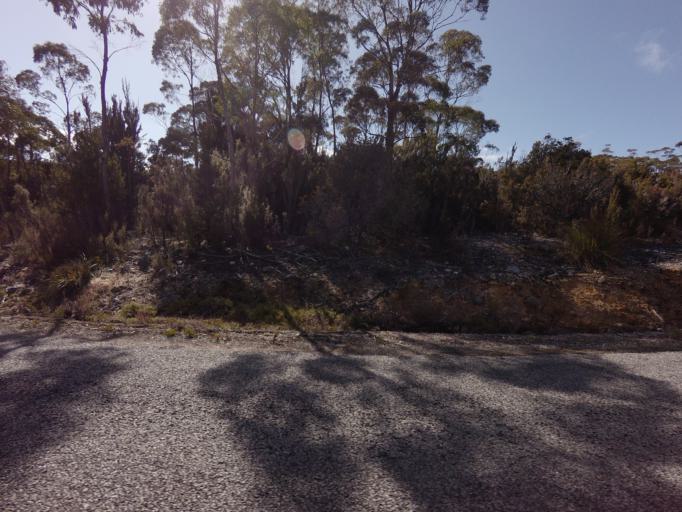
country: AU
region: Tasmania
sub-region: Huon Valley
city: Geeveston
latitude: -42.7702
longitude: 146.3967
